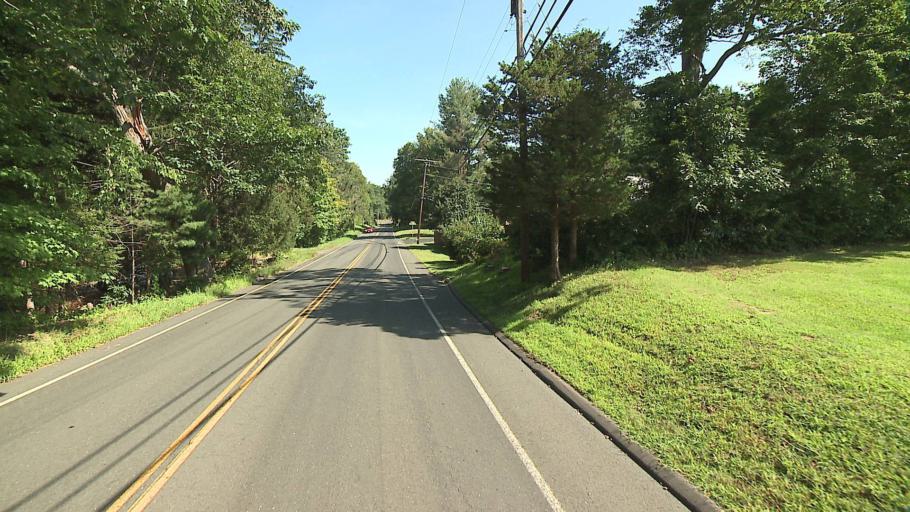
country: US
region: Connecticut
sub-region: Hartford County
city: West Simsbury
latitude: 41.8791
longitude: -72.8664
